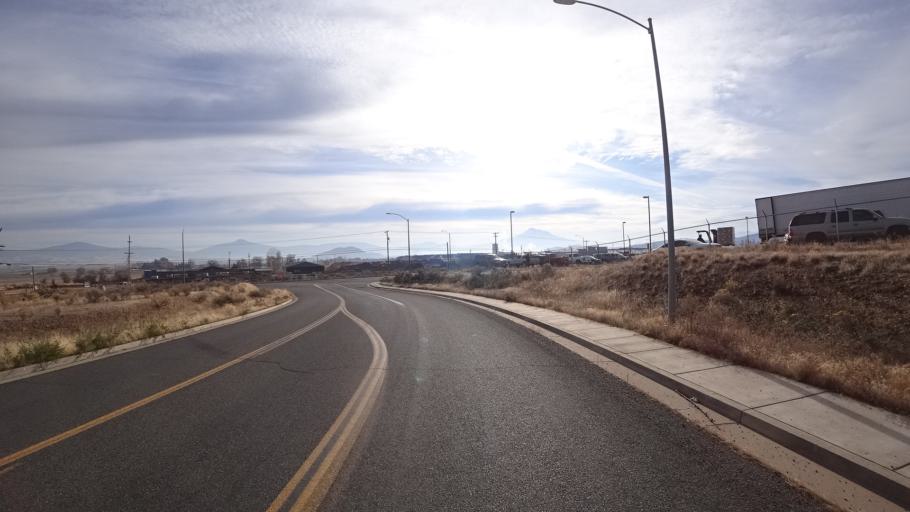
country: US
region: California
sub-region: Siskiyou County
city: Yreka
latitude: 41.7346
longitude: -122.5944
